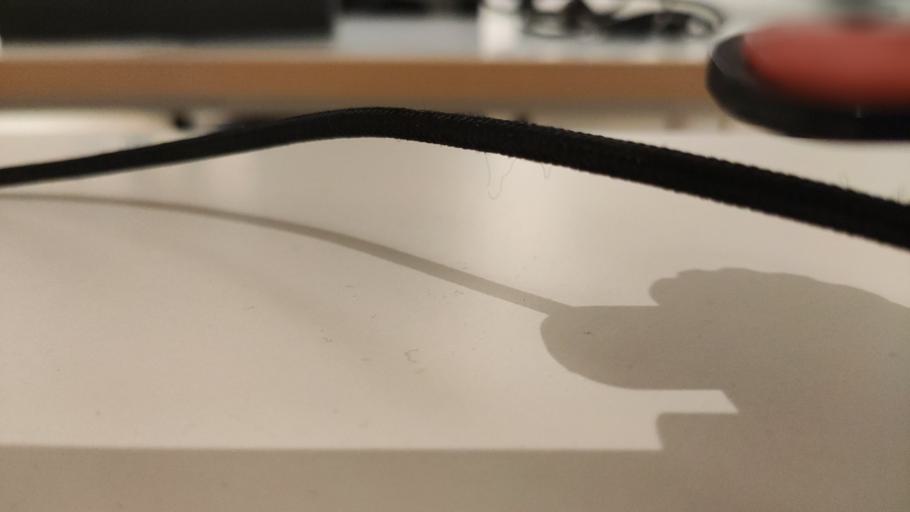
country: RU
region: Moskovskaya
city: Dorokhovo
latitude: 55.3946
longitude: 36.3877
